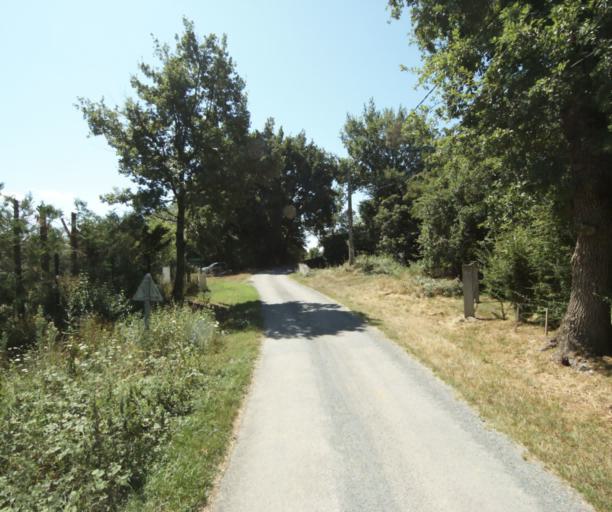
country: FR
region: Midi-Pyrenees
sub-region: Departement de la Haute-Garonne
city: Revel
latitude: 43.4924
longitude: 1.9708
